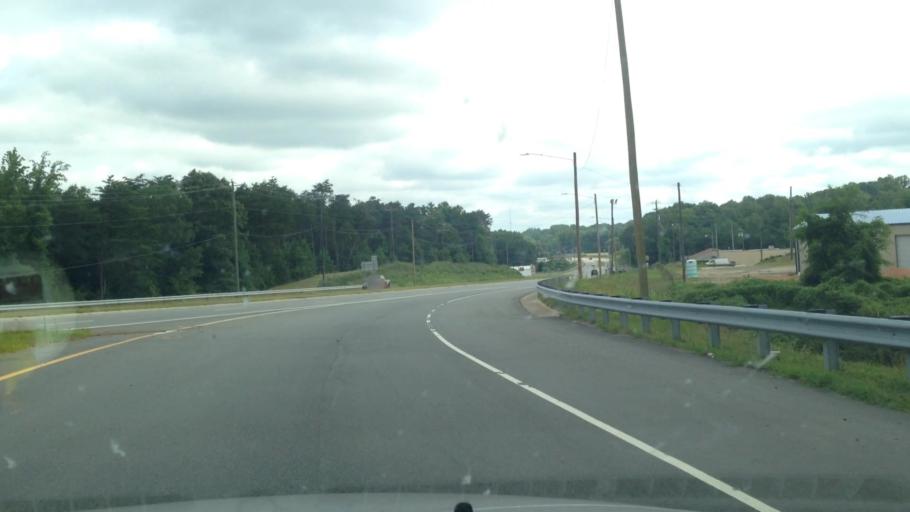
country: US
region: North Carolina
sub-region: Rockingham County
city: Reidsville
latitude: 36.3587
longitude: -79.6882
